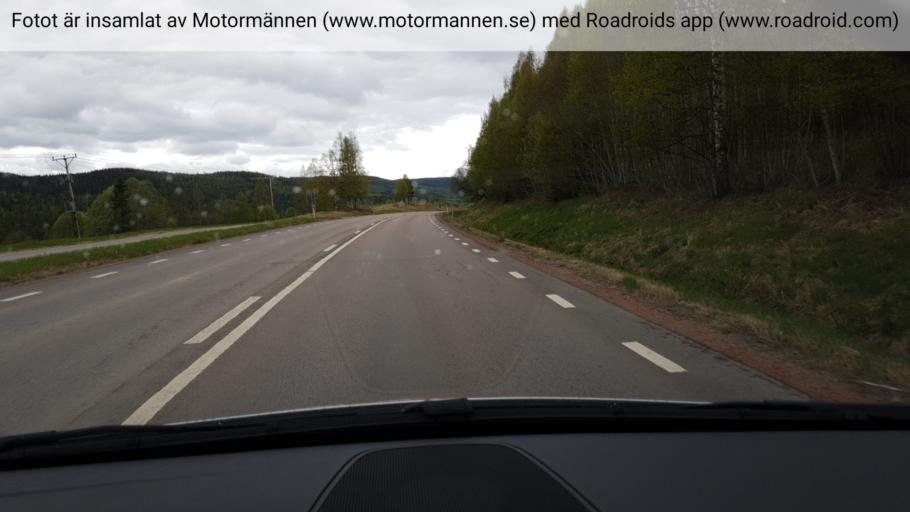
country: SE
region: Jaemtland
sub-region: Ragunda Kommun
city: Hammarstrand
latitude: 63.1511
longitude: 16.1867
